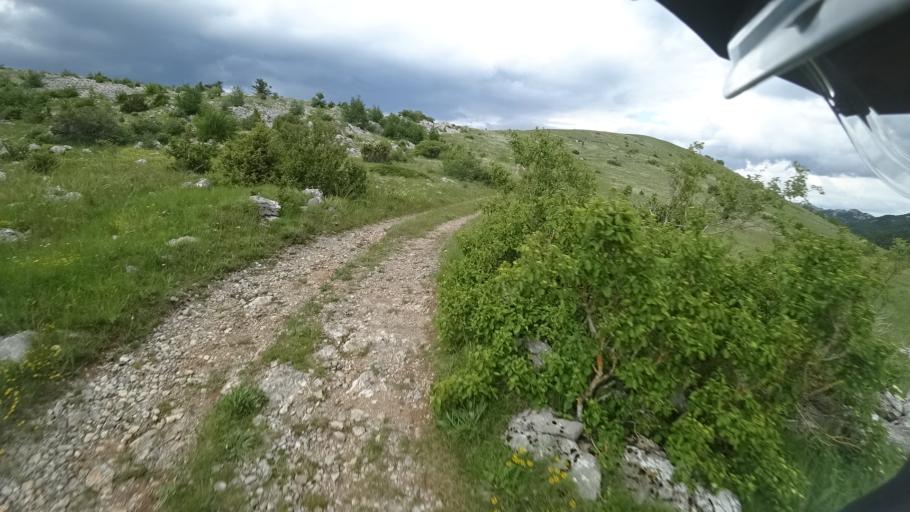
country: HR
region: Zadarska
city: Obrovac
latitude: 44.2674
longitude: 15.7263
